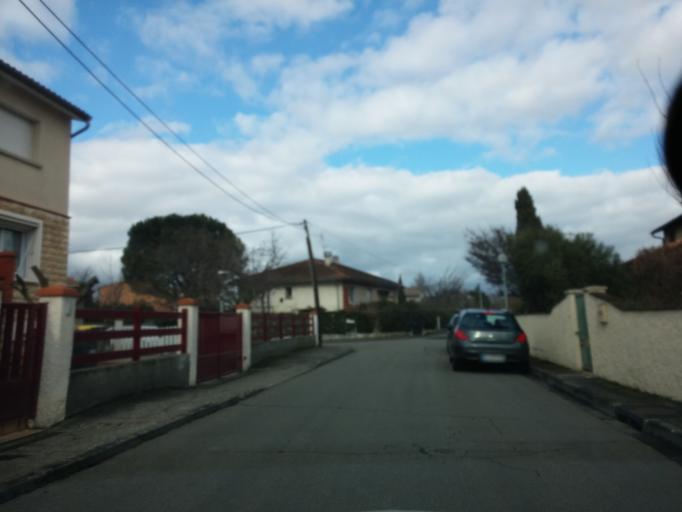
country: FR
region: Midi-Pyrenees
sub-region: Departement de la Haute-Garonne
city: Blagnac
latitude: 43.6401
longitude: 1.3982
